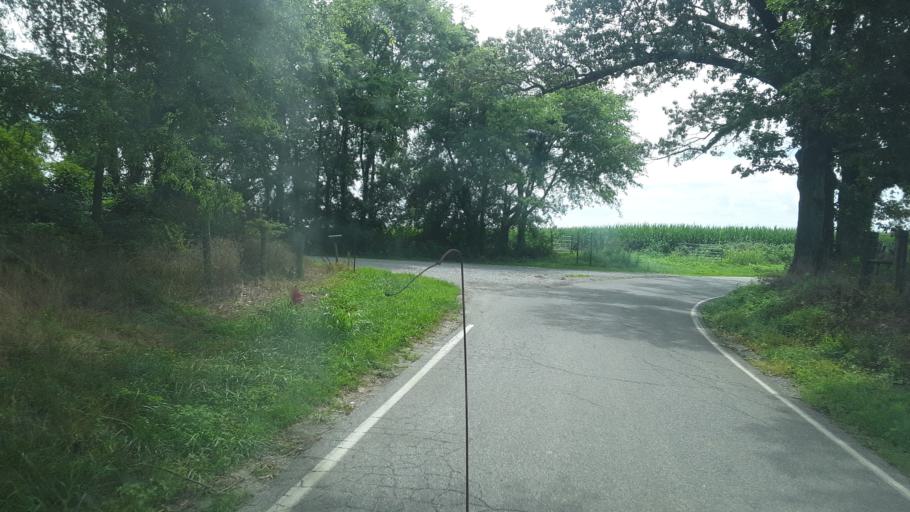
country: US
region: Kentucky
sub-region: Christian County
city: Oak Grove
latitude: 36.6574
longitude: -87.3445
